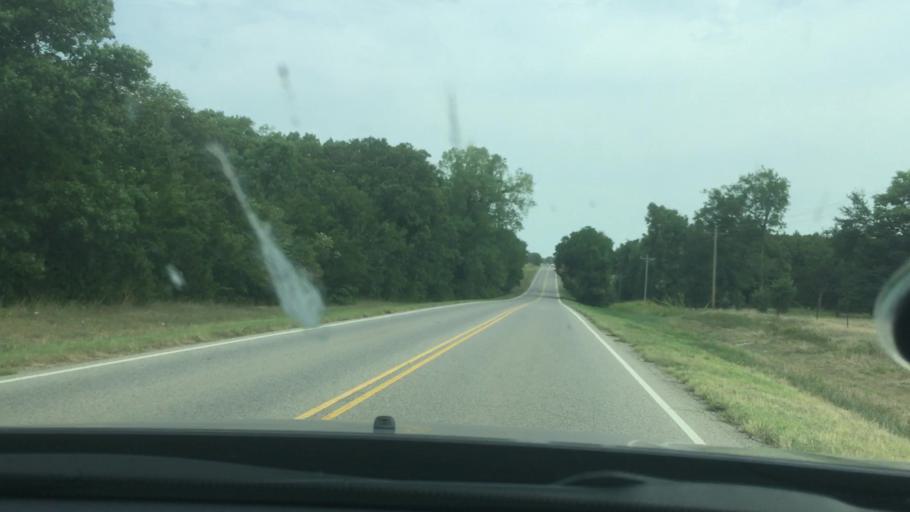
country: US
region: Oklahoma
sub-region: Bryan County
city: Durant
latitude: 34.1887
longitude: -96.4175
